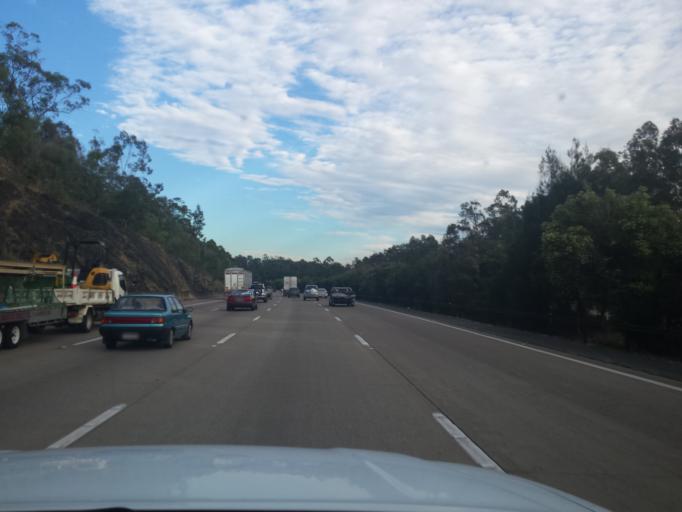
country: AU
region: Queensland
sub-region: Gold Coast
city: Ormeau Hills
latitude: -27.8252
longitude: 153.2966
